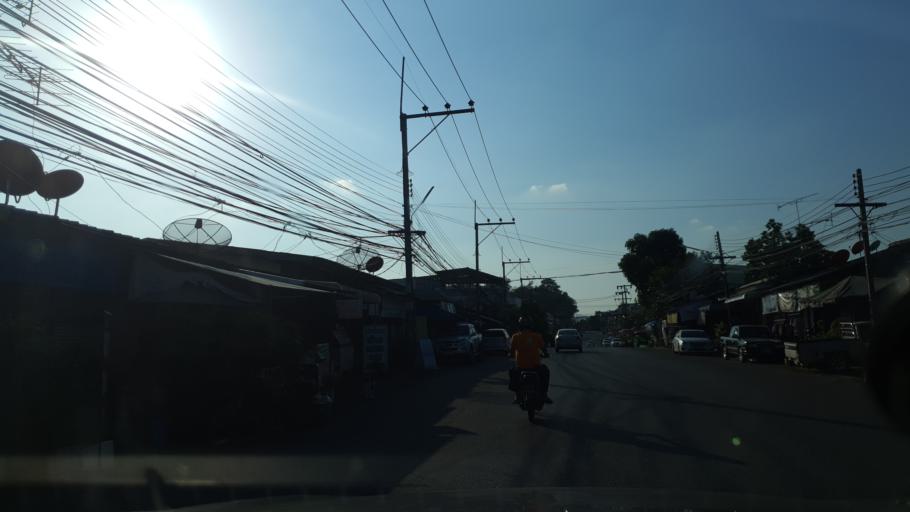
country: TH
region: Krabi
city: Krabi
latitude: 8.0806
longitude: 98.9142
